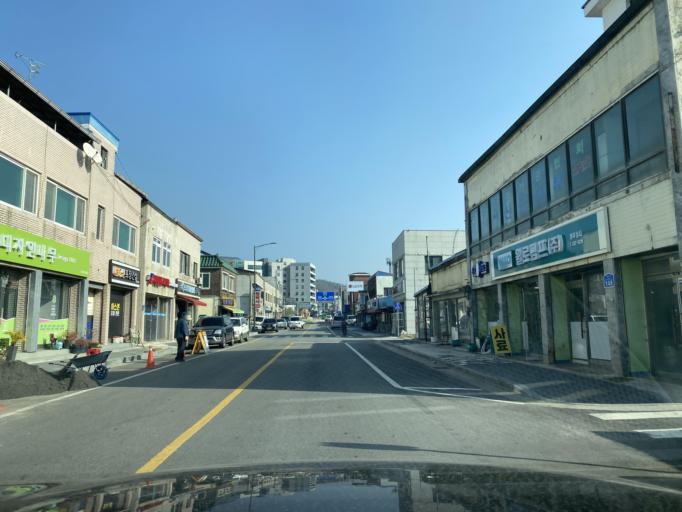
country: KR
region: Chungcheongnam-do
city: Yesan
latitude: 36.6784
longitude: 126.8413
